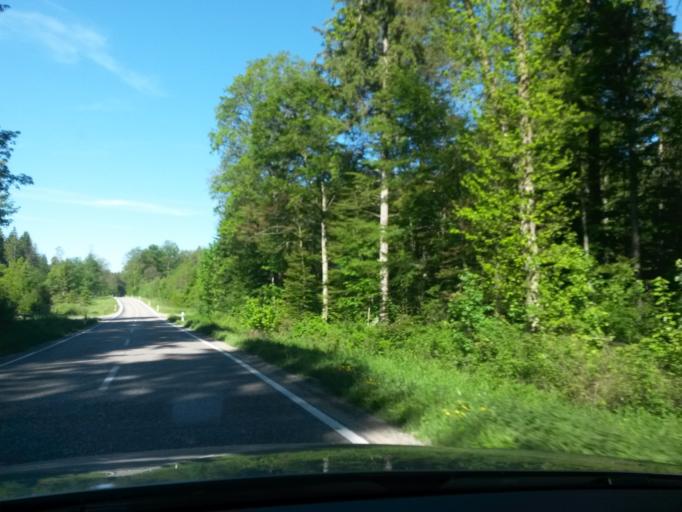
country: DE
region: Baden-Wuerttemberg
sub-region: Tuebingen Region
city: Kanzach
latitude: 48.0793
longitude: 9.5279
